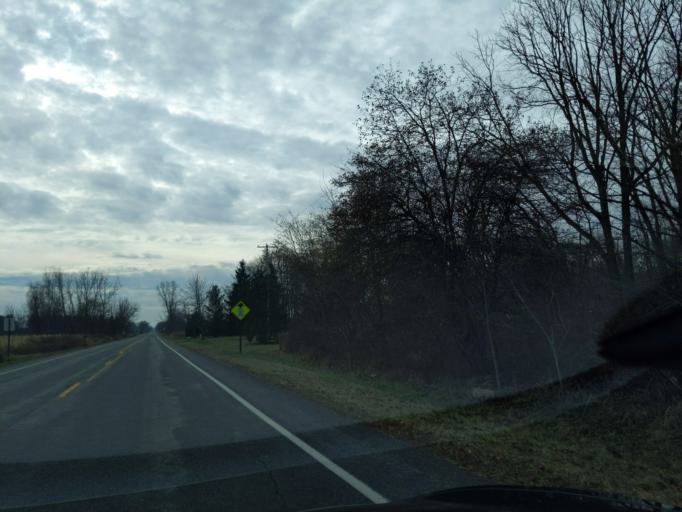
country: US
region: Michigan
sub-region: Ingham County
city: Holt
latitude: 42.5913
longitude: -84.5230
